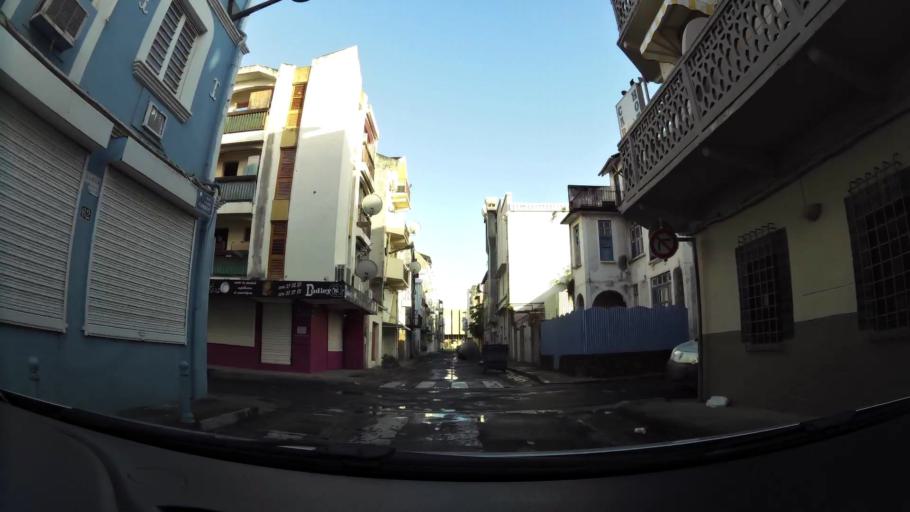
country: MQ
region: Martinique
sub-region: Martinique
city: Fort-de-France
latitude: 14.6049
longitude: -61.0668
